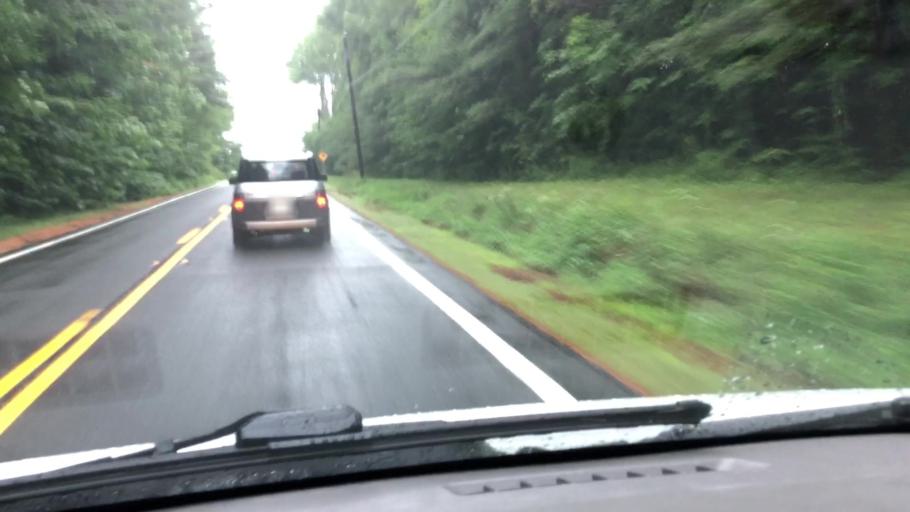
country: US
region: Massachusetts
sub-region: Hampshire County
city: Chesterfield
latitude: 42.3784
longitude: -72.9218
